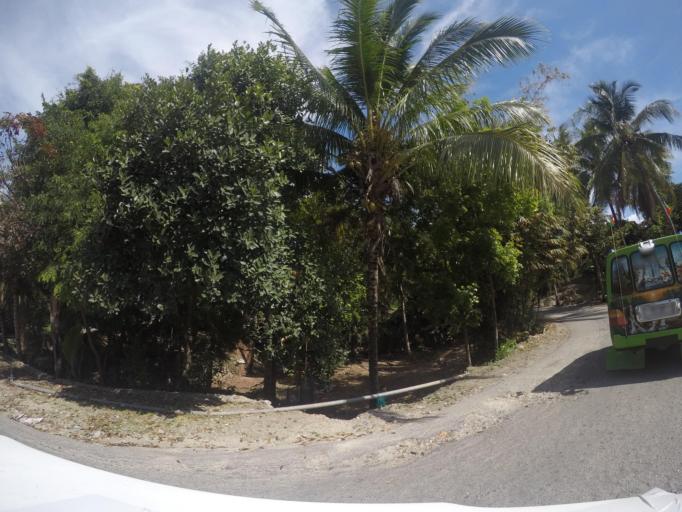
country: TL
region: Baucau
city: Baucau
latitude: -8.4669
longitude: 126.4599
